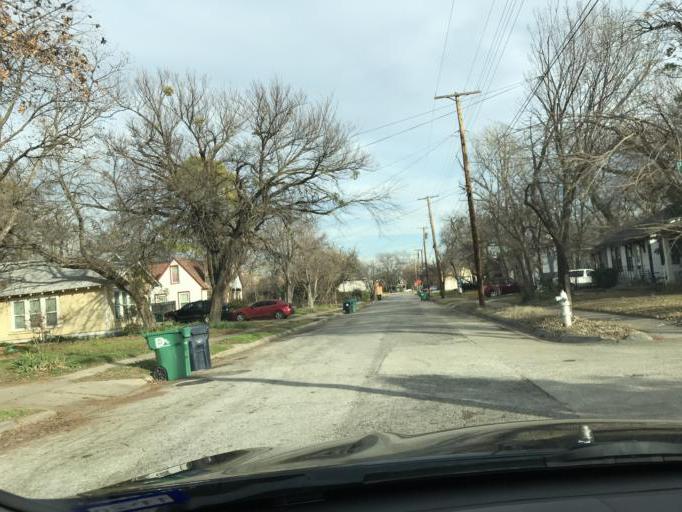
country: US
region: Texas
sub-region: Denton County
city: Denton
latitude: 33.2117
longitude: -97.1358
